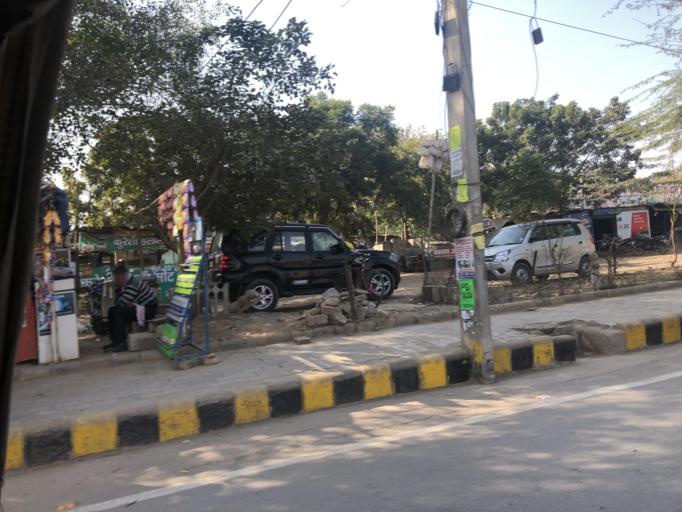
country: IN
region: Haryana
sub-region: Gurgaon
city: Gurgaon
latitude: 28.4480
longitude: 77.0740
